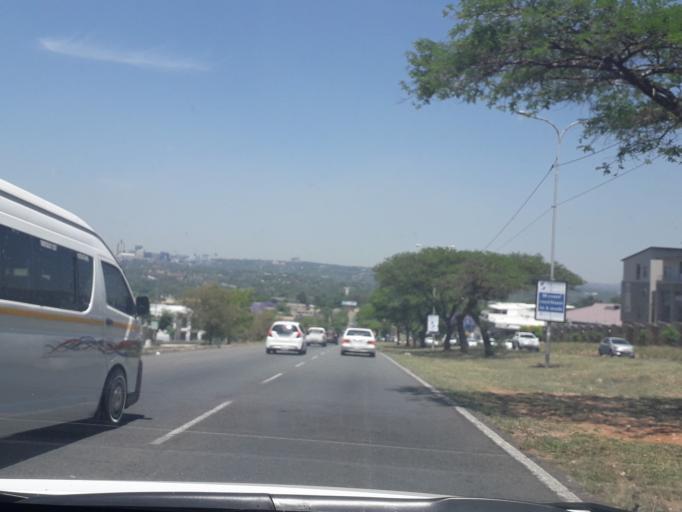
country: ZA
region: Gauteng
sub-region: City of Johannesburg Metropolitan Municipality
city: Midrand
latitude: -26.0652
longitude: 28.0247
